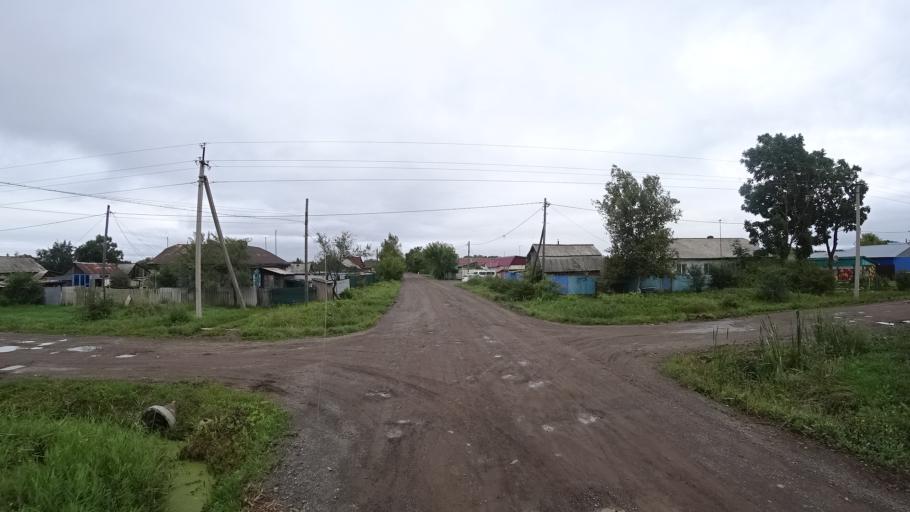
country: RU
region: Primorskiy
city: Chernigovka
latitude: 44.3496
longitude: 132.5734
